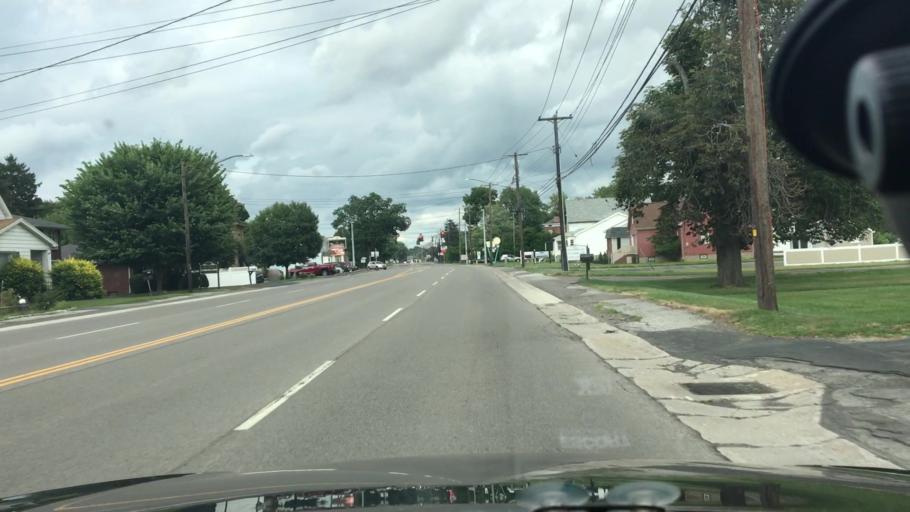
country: US
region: New York
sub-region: Erie County
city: West Seneca
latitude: 42.8293
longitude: -78.7667
